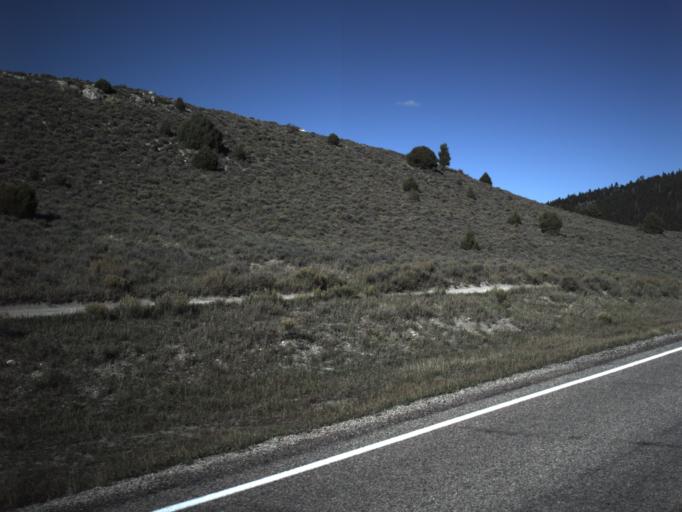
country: US
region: Utah
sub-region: Garfield County
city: Panguitch
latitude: 37.7064
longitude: -112.6337
